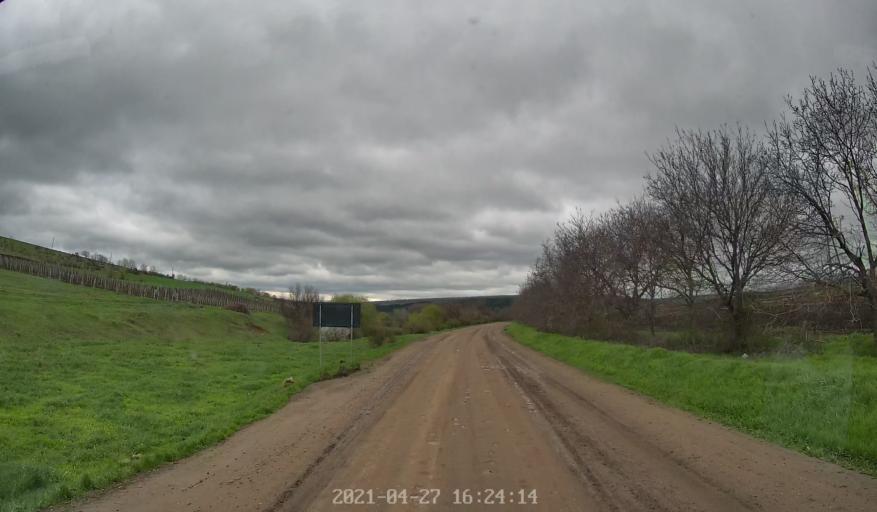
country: MD
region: Chisinau
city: Singera
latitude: 46.9934
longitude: 29.0207
